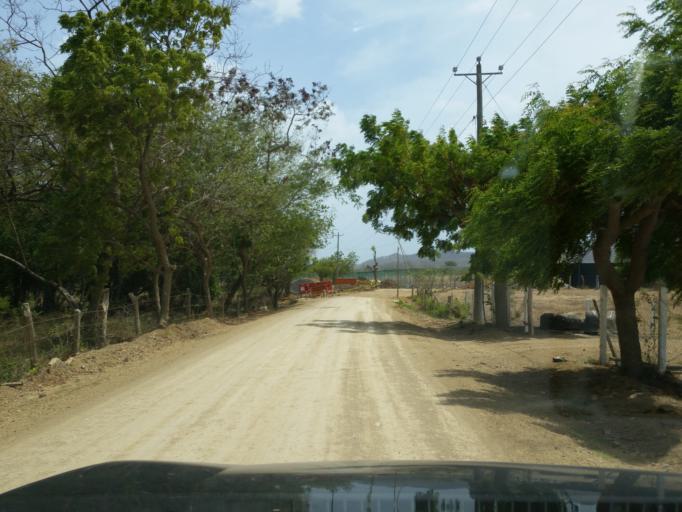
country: NI
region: Rivas
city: Tola
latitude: 11.4214
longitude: -86.0345
